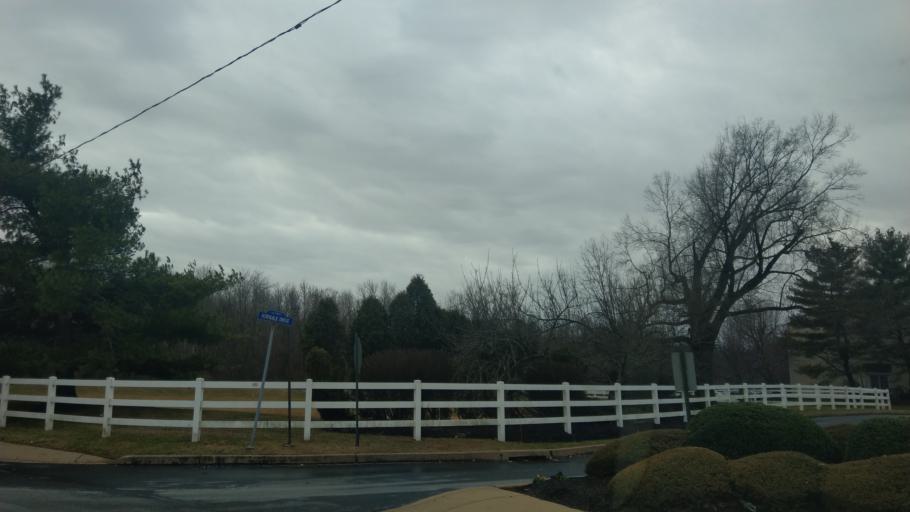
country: US
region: Pennsylvania
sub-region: Bucks County
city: Bristol
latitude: 40.1284
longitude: -74.8675
